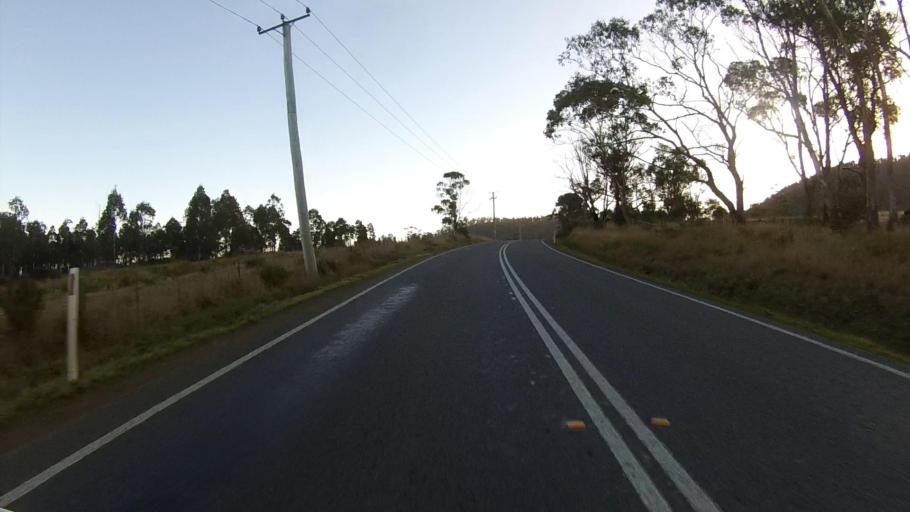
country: AU
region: Tasmania
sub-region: Sorell
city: Sorell
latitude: -42.8164
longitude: 147.7607
